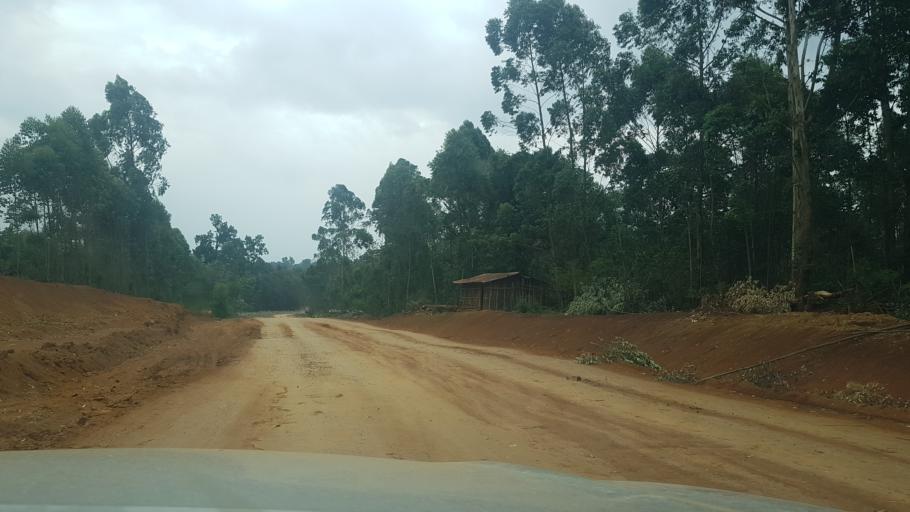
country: ET
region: Oromiya
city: Gore
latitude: 7.8995
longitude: 35.4971
